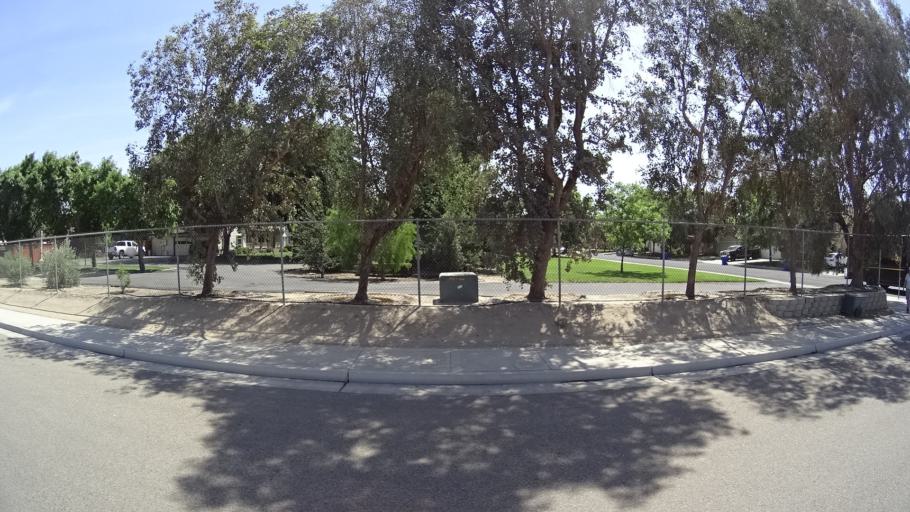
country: US
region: California
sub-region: Kings County
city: Lucerne
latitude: 36.3457
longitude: -119.6821
